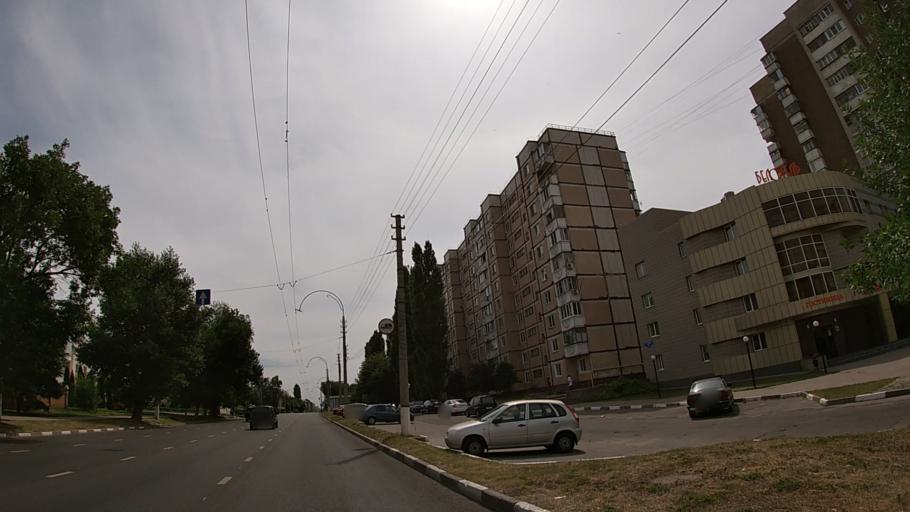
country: RU
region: Belgorod
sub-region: Belgorodskiy Rayon
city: Belgorod
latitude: 50.5999
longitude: 36.5703
